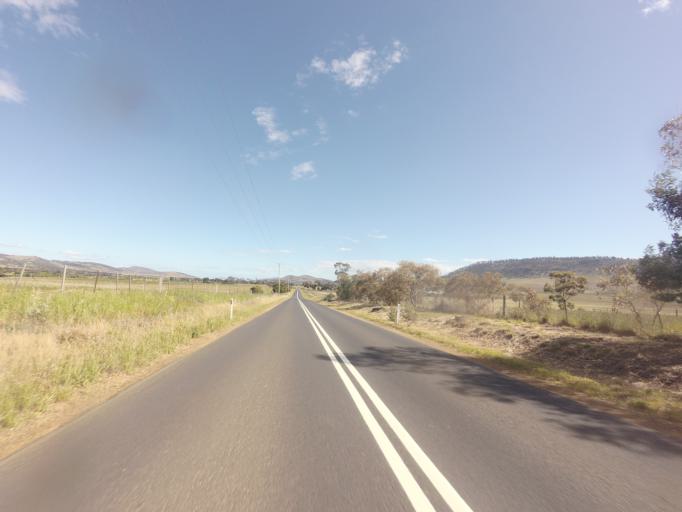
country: AU
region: Tasmania
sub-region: Clarence
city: Cambridge
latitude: -42.6941
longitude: 147.4290
